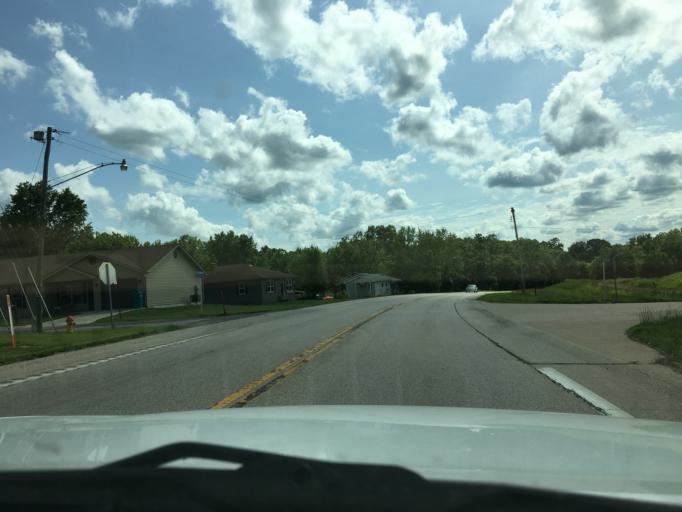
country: US
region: Missouri
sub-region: Franklin County
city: Gerald
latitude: 38.3954
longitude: -91.3403
